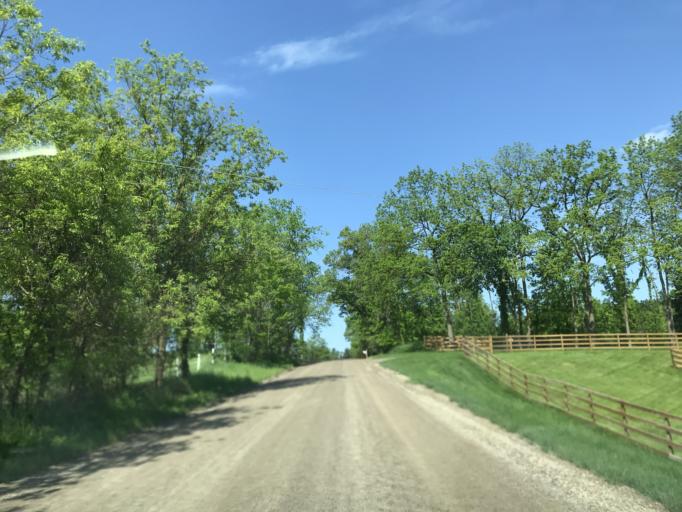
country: US
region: Michigan
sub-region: Oakland County
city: South Lyon
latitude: 42.4810
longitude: -83.6921
